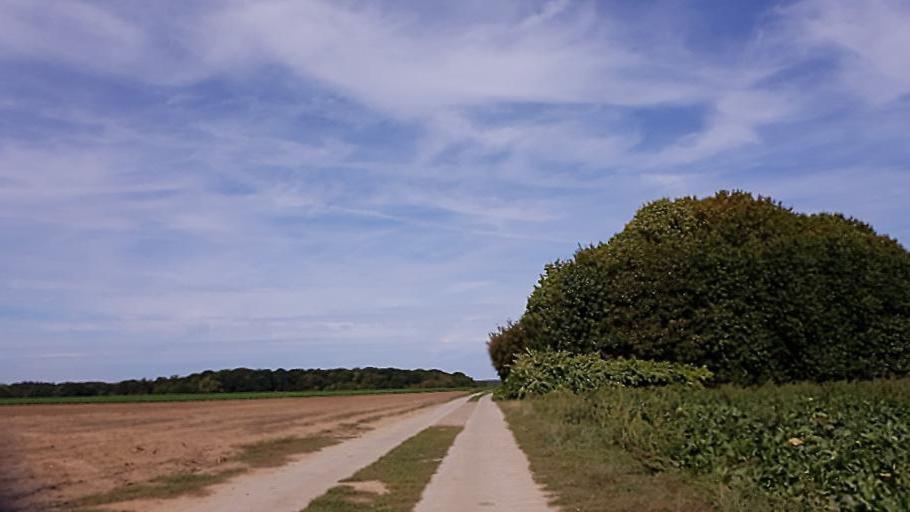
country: BE
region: Wallonia
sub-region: Province du Brabant Wallon
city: Grez-Doiceau
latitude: 50.7705
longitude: 4.6860
